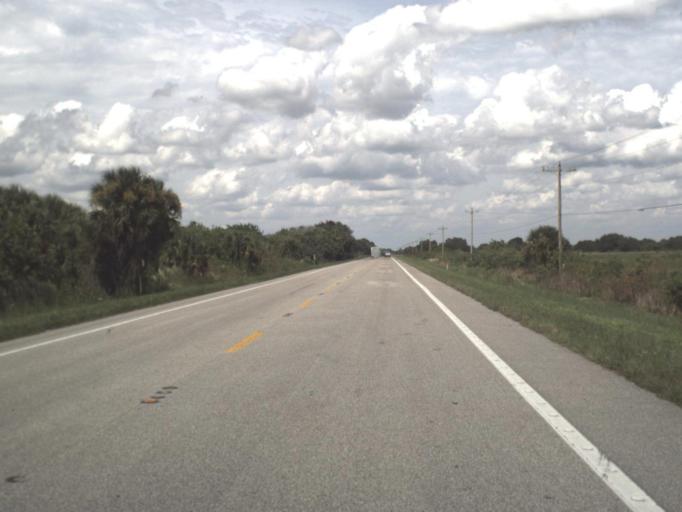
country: US
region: Florida
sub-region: Collier County
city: Immokalee
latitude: 26.5722
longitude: -81.4363
